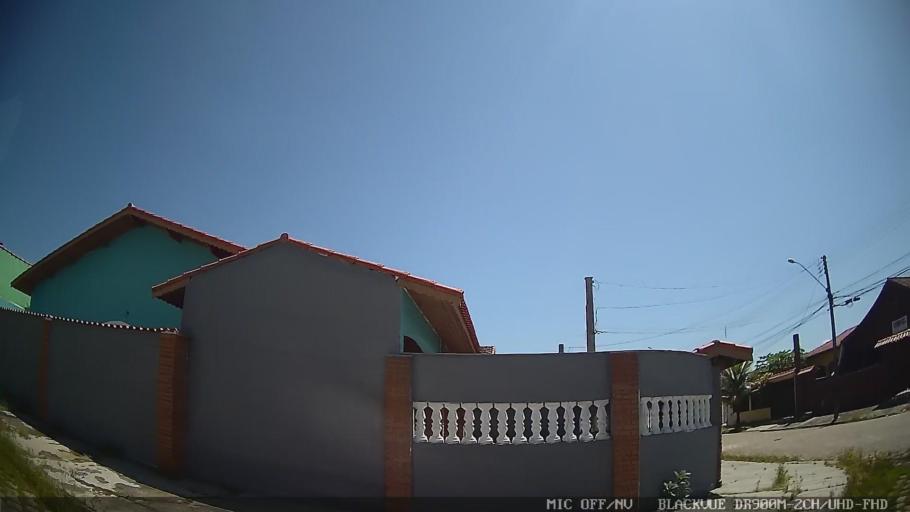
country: BR
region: Sao Paulo
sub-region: Peruibe
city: Peruibe
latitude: -24.2851
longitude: -46.9635
